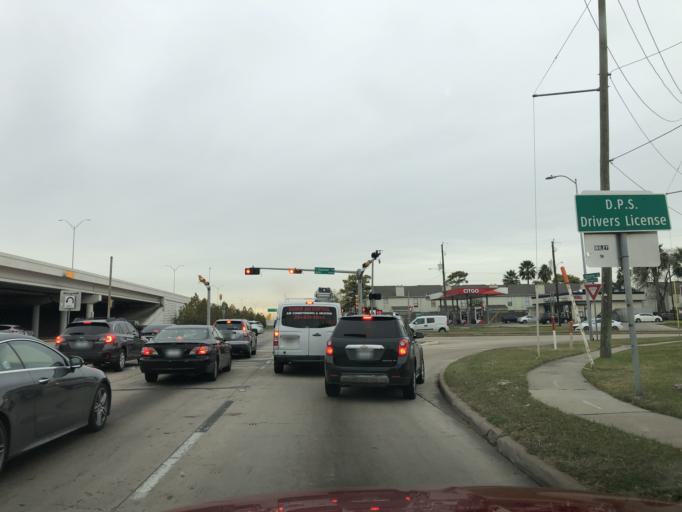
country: US
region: Texas
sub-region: Fort Bend County
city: Missouri City
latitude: 29.6371
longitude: -95.5302
